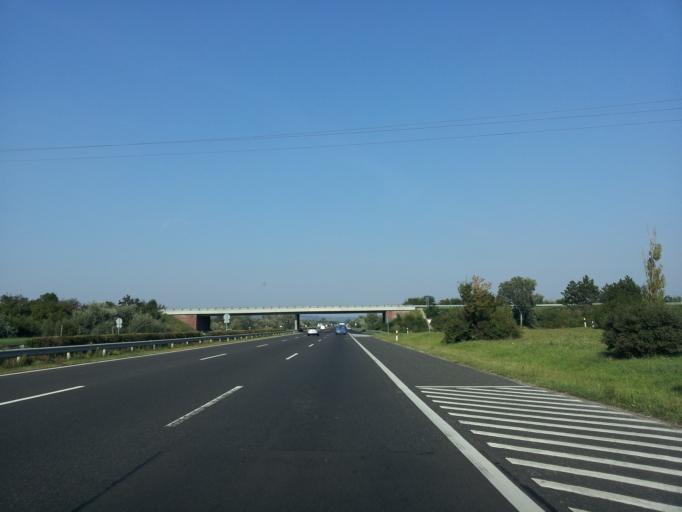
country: HU
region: Fejer
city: Pakozd
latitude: 47.1918
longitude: 18.5072
